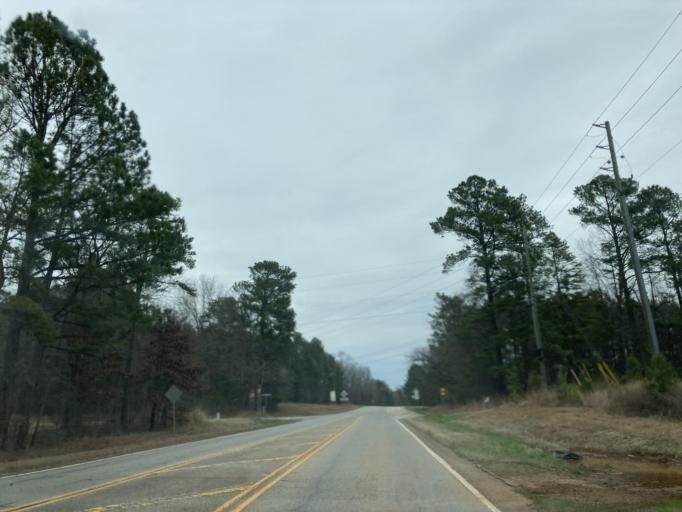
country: US
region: Georgia
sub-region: Jones County
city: Gray
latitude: 32.9882
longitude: -83.6026
